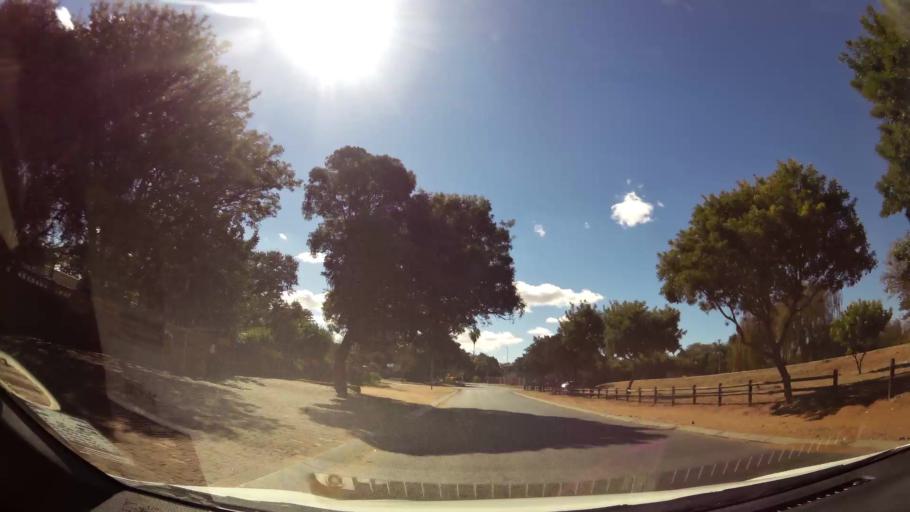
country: ZA
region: Limpopo
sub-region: Capricorn District Municipality
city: Polokwane
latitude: -23.9140
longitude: 29.4773
